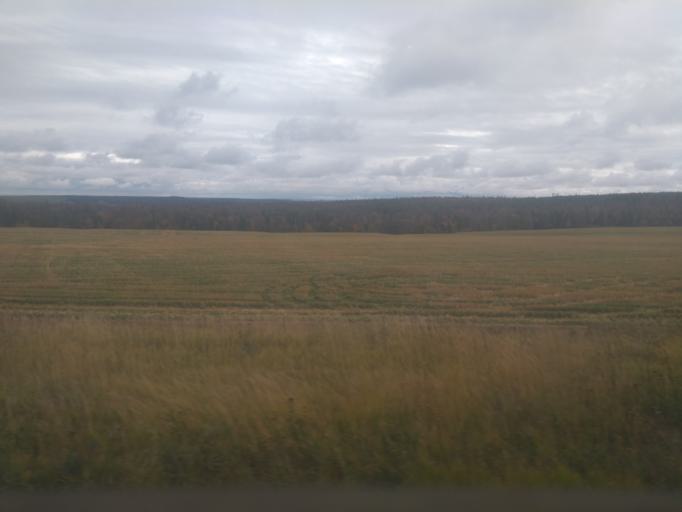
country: RU
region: Udmurtiya
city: Alnashi
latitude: 56.1426
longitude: 52.5720
